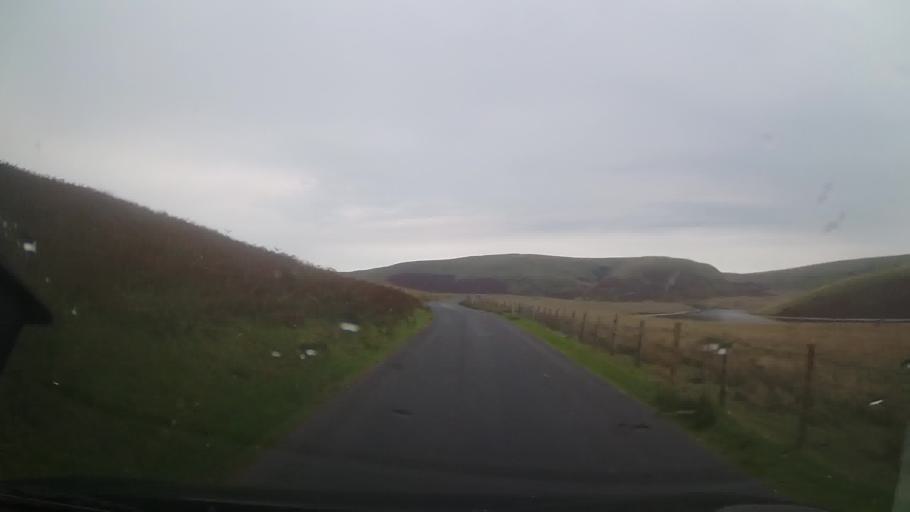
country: GB
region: Wales
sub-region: Sir Powys
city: Rhayader
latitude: 52.3233
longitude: -3.6262
